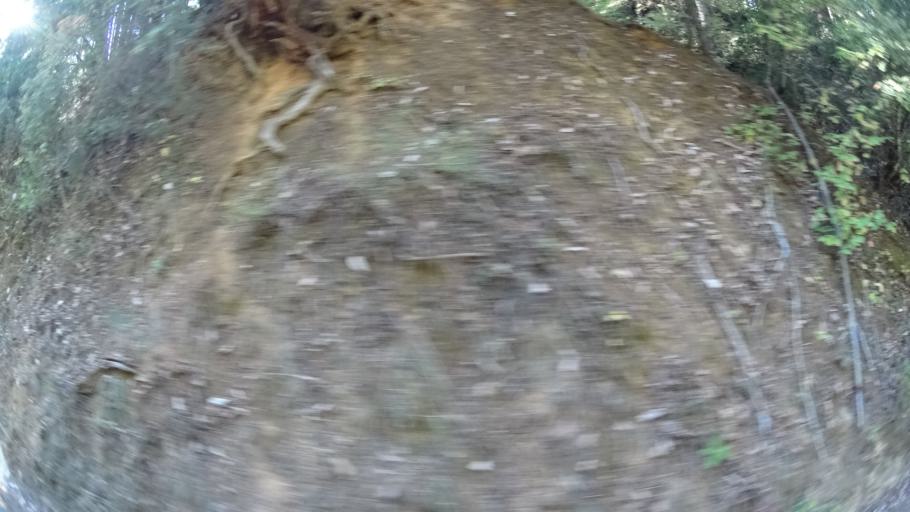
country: US
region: California
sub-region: Siskiyou County
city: Happy Camp
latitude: 41.3162
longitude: -123.1798
